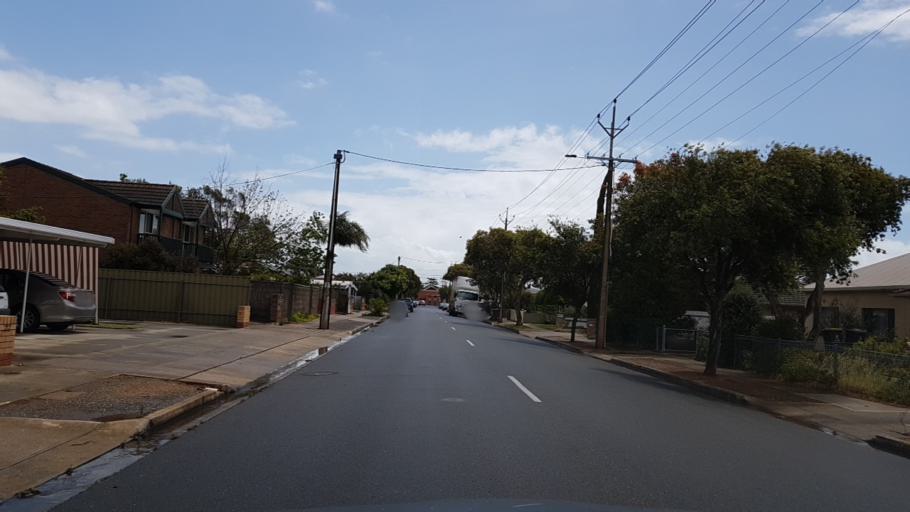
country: AU
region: South Australia
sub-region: Marion
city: South Plympton
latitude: -34.9868
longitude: 138.5595
